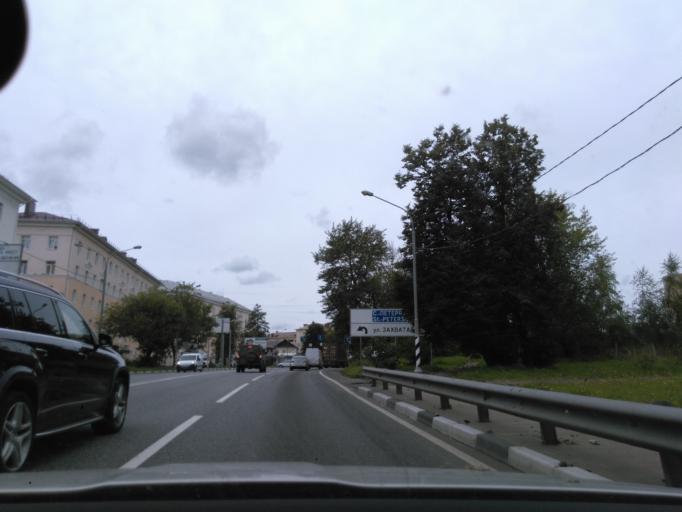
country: RU
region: Moskovskaya
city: Klin
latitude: 56.3301
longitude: 36.7331
